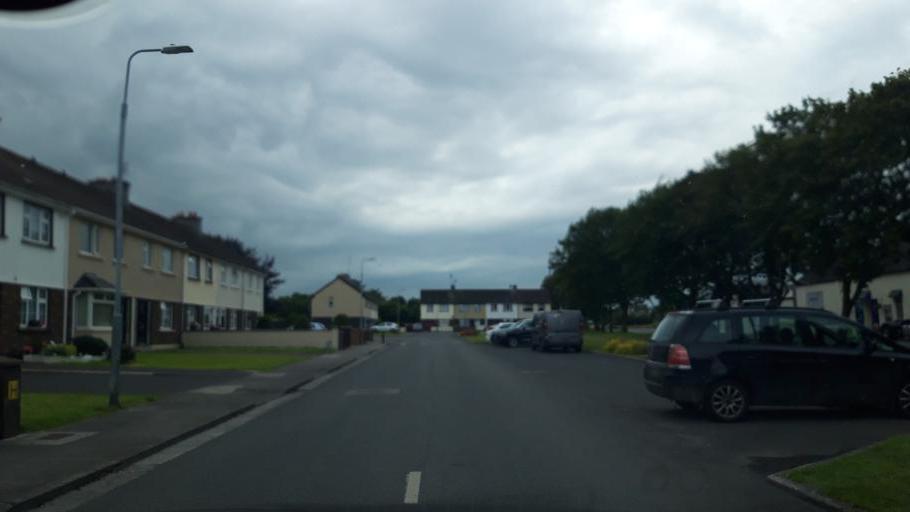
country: IE
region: Leinster
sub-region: Kilkenny
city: Ballyragget
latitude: 52.7314
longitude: -7.4051
